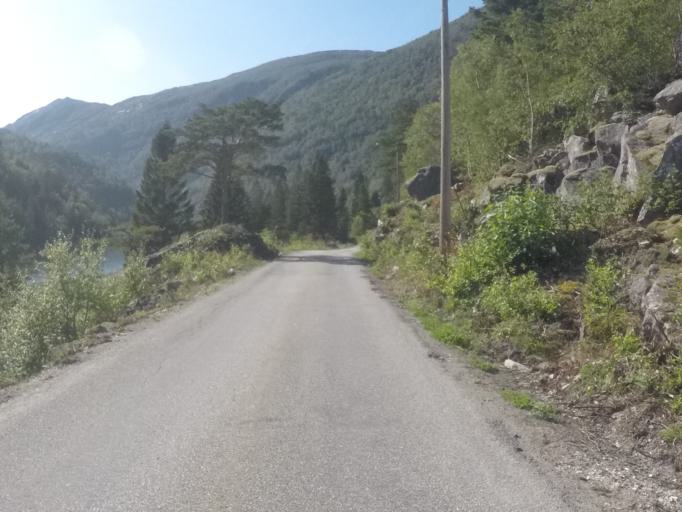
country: NO
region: Hordaland
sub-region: Odda
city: Odda
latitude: 60.1316
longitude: 6.6343
